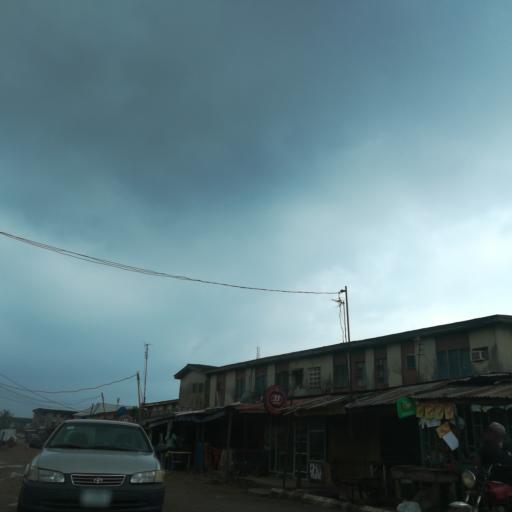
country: NG
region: Lagos
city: Agege
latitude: 6.5987
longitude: 3.3001
